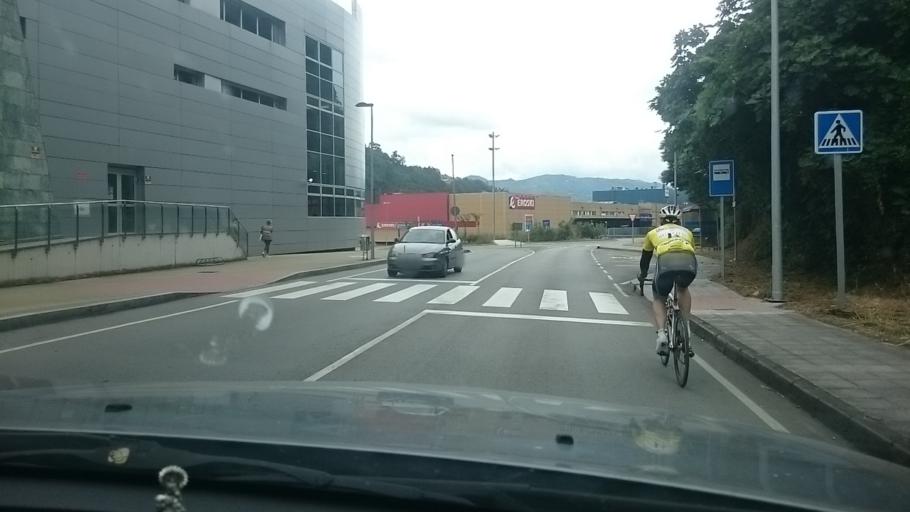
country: ES
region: Asturias
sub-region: Province of Asturias
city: Mieres
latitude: 43.2267
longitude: -5.7809
